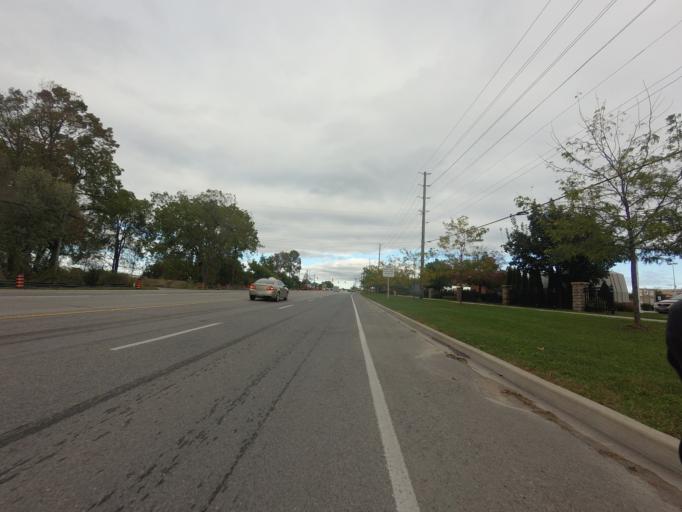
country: CA
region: Ontario
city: Cobourg
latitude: 43.9700
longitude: -78.2047
